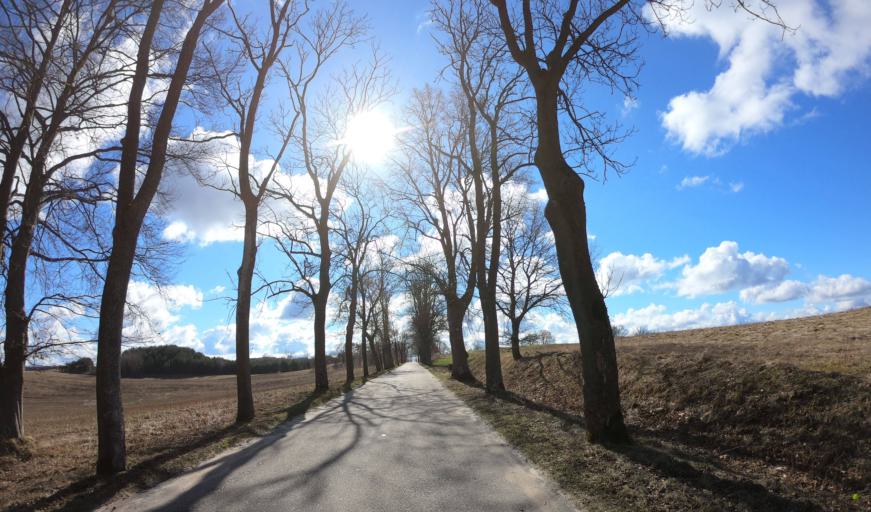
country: PL
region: West Pomeranian Voivodeship
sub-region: Powiat drawski
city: Zlocieniec
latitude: 53.4722
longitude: 15.9692
